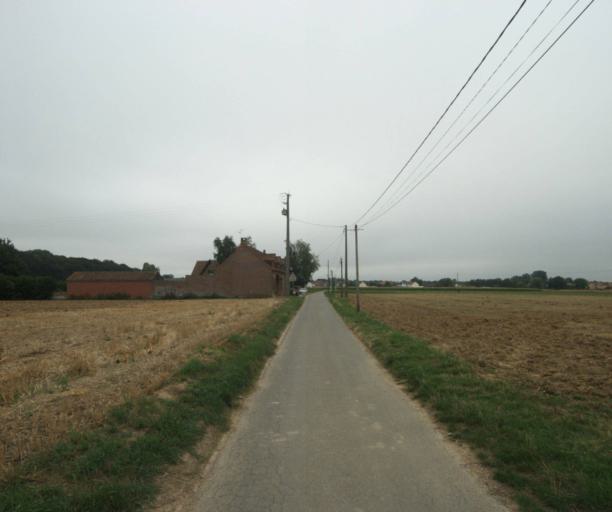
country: FR
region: Nord-Pas-de-Calais
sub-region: Departement du Nord
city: Baisieux
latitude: 50.6178
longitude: 3.2518
